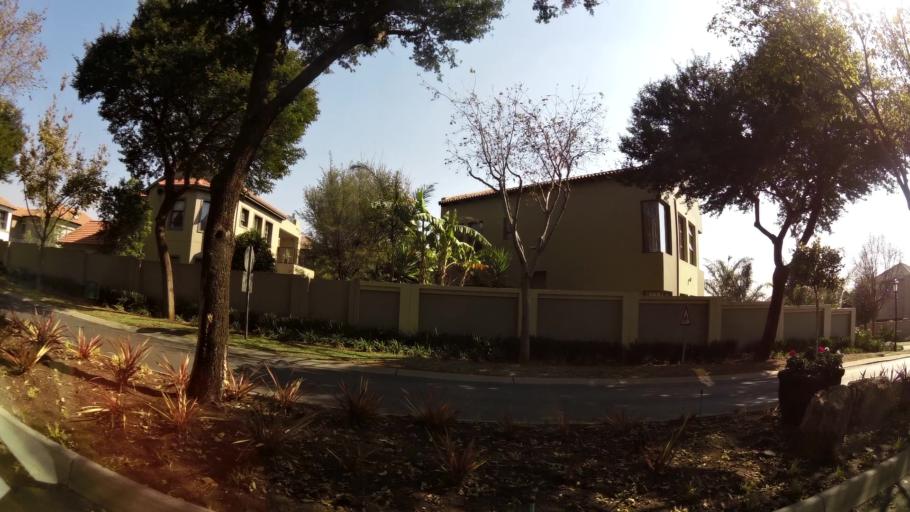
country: ZA
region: Gauteng
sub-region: City of Johannesburg Metropolitan Municipality
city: Modderfontein
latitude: -26.1156
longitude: 28.1551
